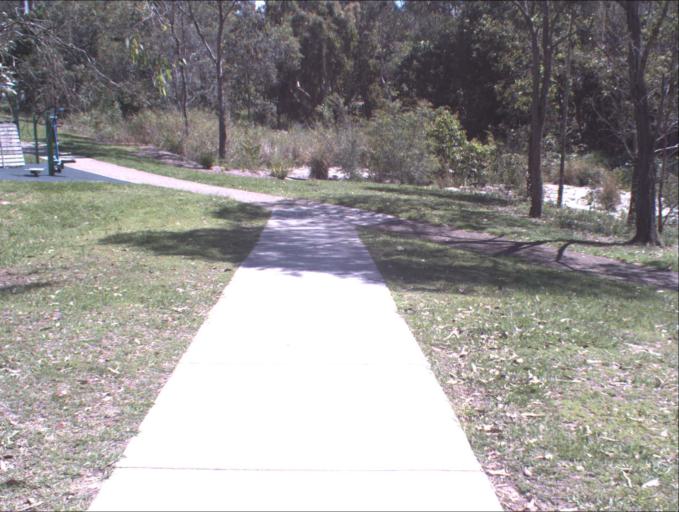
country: AU
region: Queensland
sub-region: Logan
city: Beenleigh
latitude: -27.7038
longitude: 153.1723
